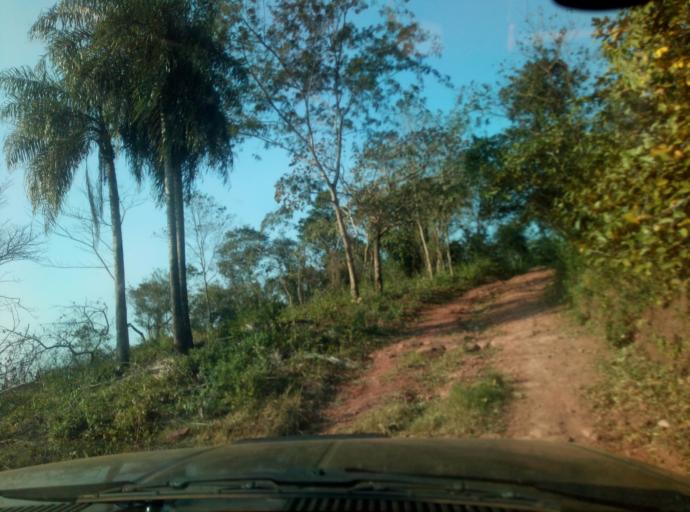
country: PY
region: Caaguazu
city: San Joaquin
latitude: -25.1560
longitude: -56.1213
